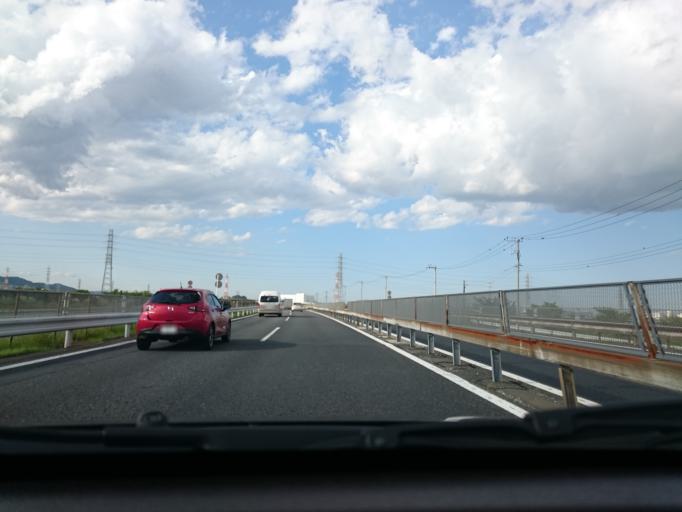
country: JP
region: Kanagawa
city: Isehara
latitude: 35.3934
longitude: 139.3342
